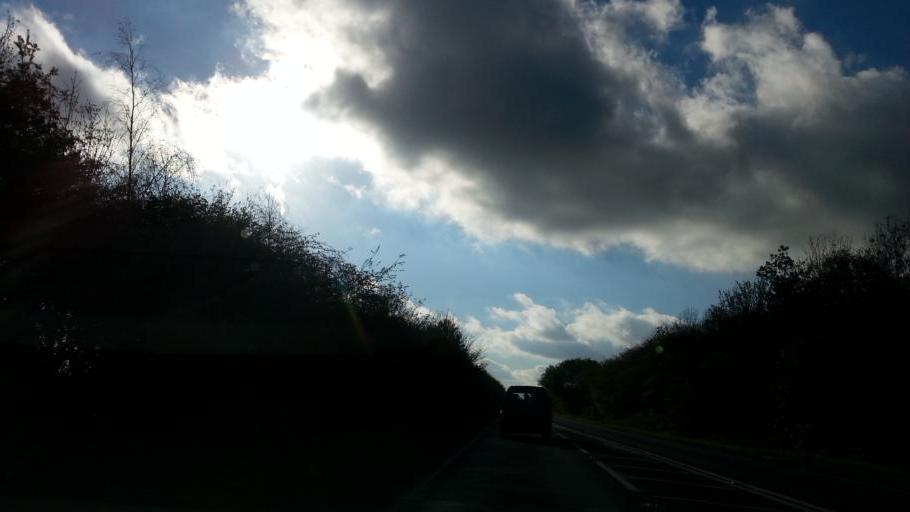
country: GB
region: England
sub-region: Norfolk
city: Harleston
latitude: 52.3920
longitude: 1.2757
